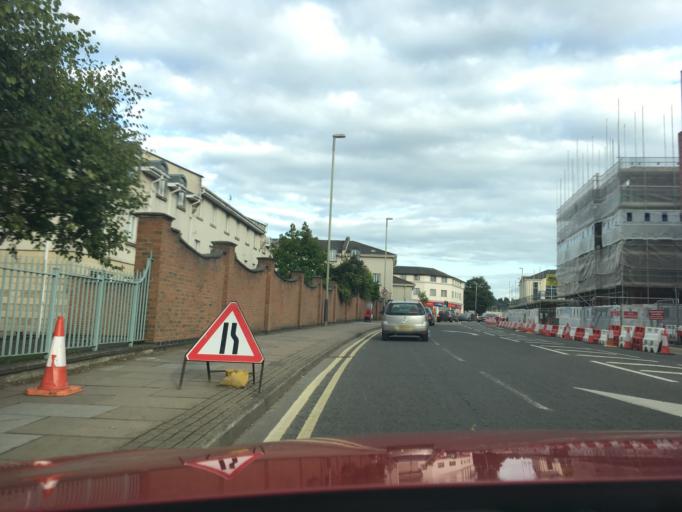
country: GB
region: England
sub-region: Gloucestershire
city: Cheltenham
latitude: 51.9022
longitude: -2.0710
